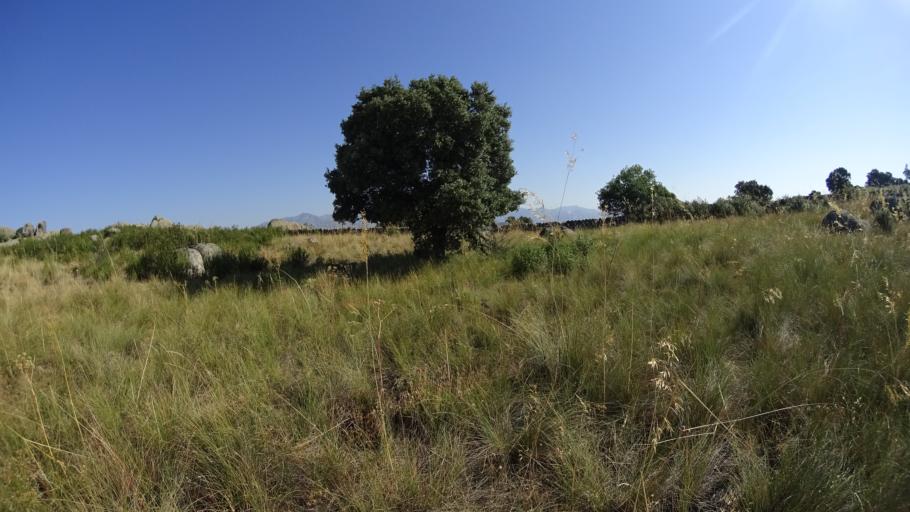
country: ES
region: Madrid
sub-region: Provincia de Madrid
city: Moralzarzal
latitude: 40.6504
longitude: -3.9441
